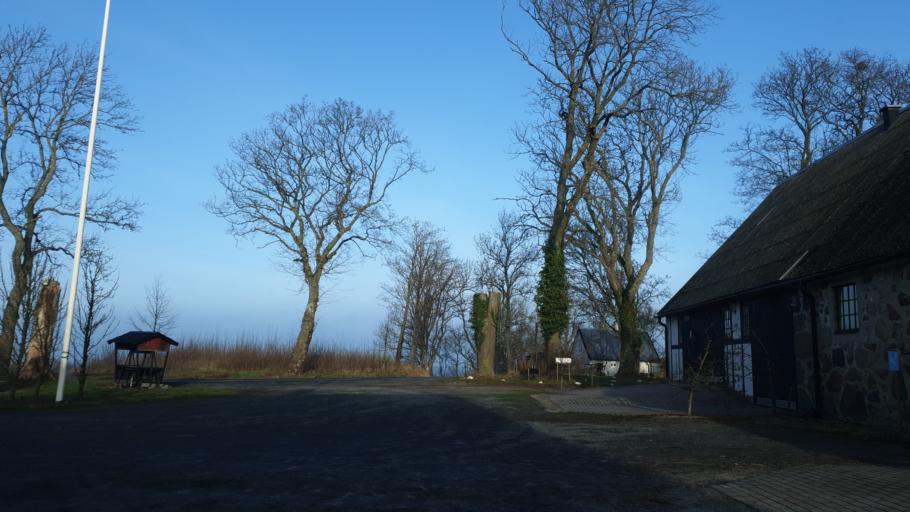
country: SE
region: Skane
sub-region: Simrishamns Kommun
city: Kivik
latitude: 55.6783
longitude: 14.2388
